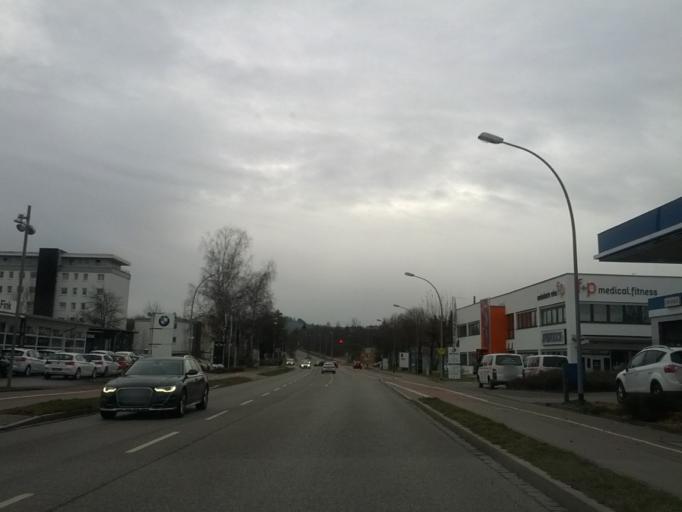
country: DE
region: Bavaria
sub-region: Swabia
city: Kempten (Allgaeu)
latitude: 47.7170
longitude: 10.2958
